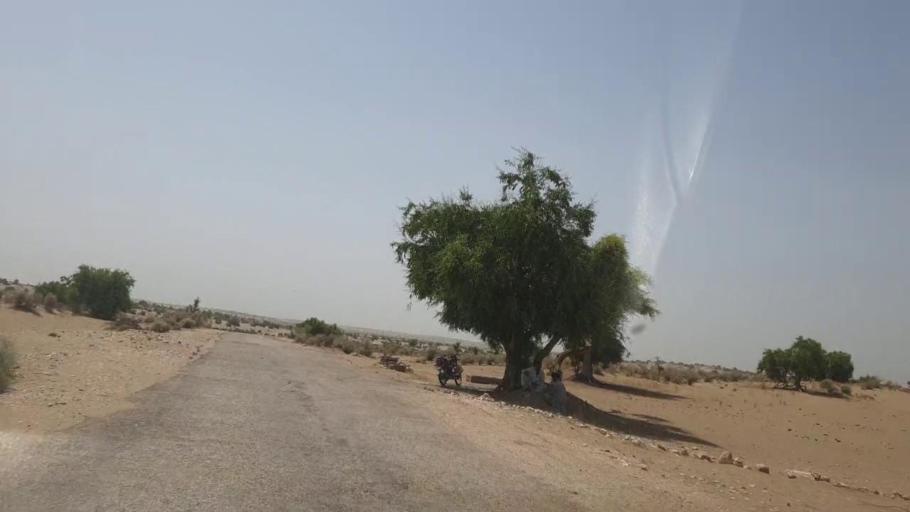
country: PK
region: Sindh
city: Khanpur
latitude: 27.3605
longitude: 69.3148
